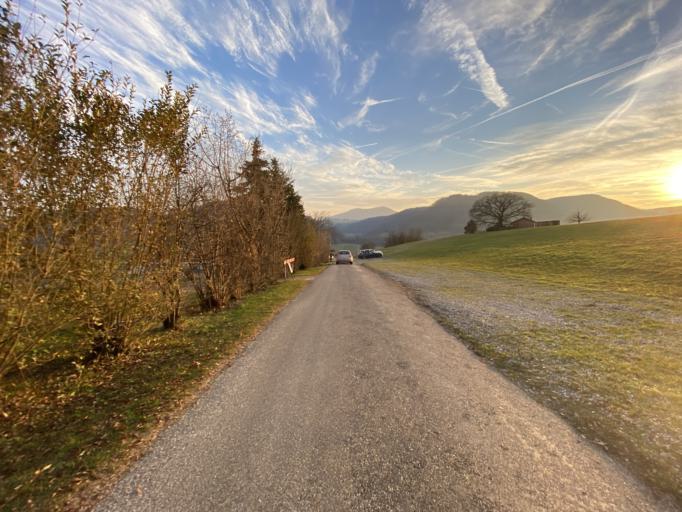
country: CH
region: Aargau
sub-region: Bezirk Laufenburg
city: Frick
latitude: 47.5077
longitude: 8.0405
